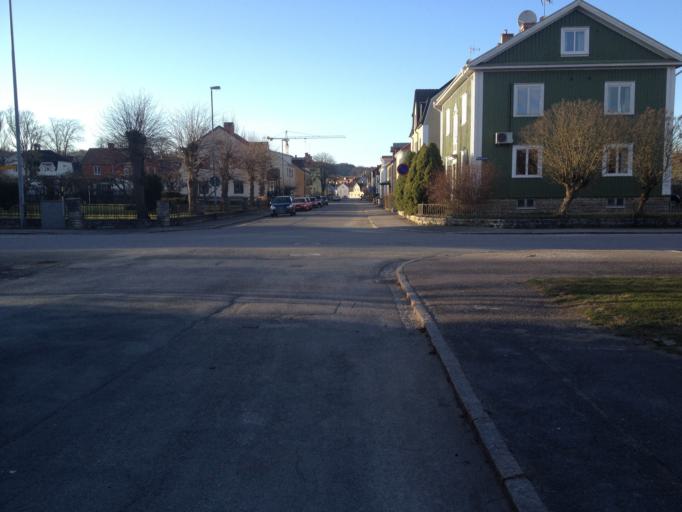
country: SE
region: Vaestra Goetaland
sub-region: Falkopings Kommun
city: Falkoeping
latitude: 58.1699
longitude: 13.5550
